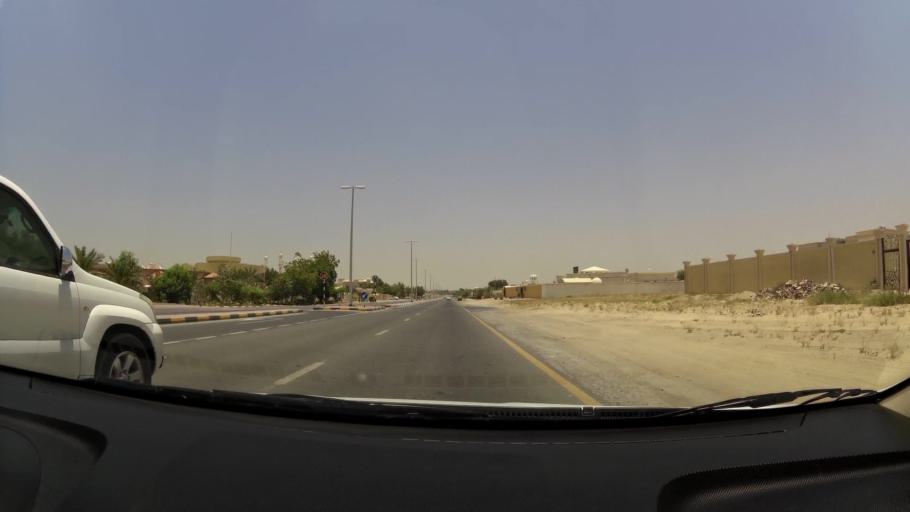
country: AE
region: Ajman
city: Ajman
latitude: 25.4121
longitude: 55.4877
